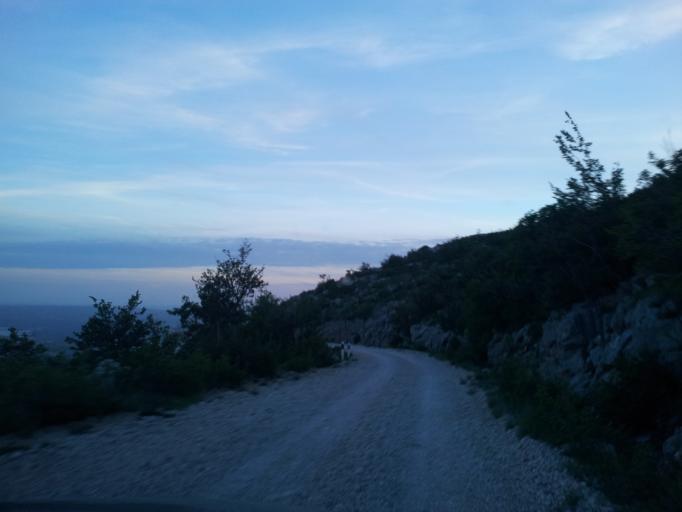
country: HR
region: Zadarska
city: Krusevo
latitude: 44.2523
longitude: 15.6325
